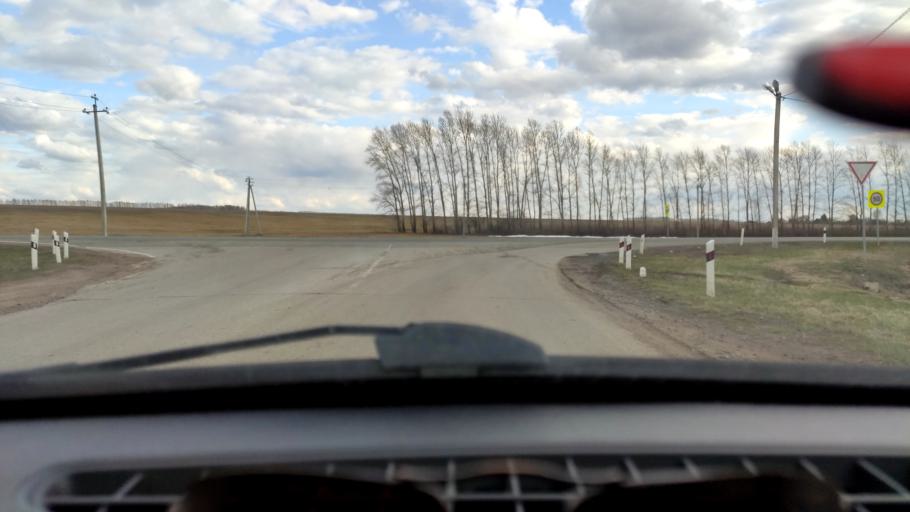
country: RU
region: Bashkortostan
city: Karmaskaly
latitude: 54.3897
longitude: 56.2389
